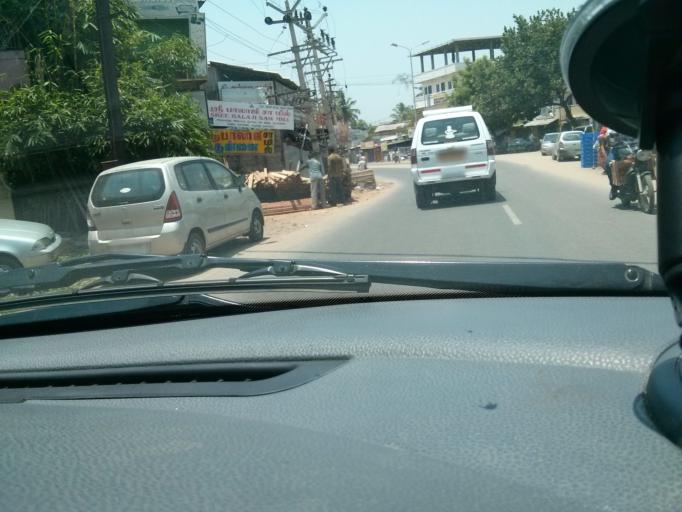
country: IN
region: Tamil Nadu
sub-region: Coimbatore
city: Coimbatore
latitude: 11.0364
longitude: 76.9530
